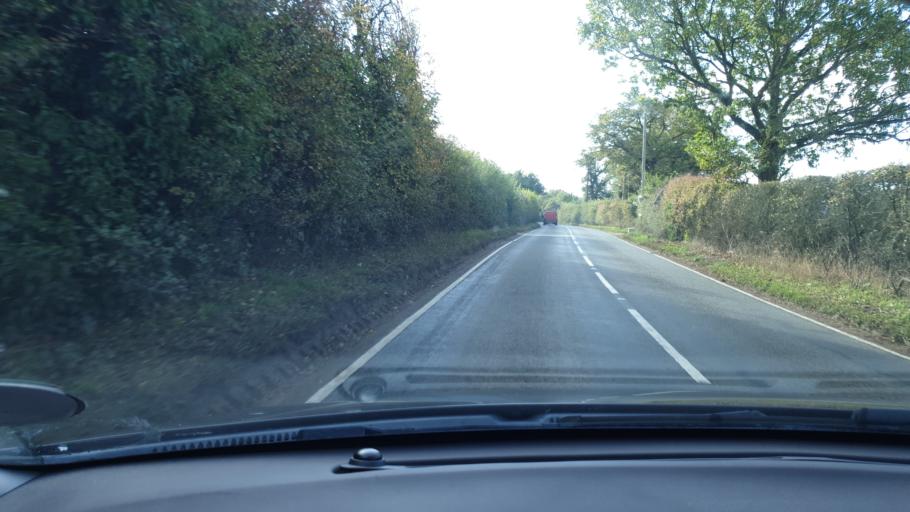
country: GB
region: England
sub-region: Essex
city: Great Bentley
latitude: 51.8535
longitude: 1.0351
